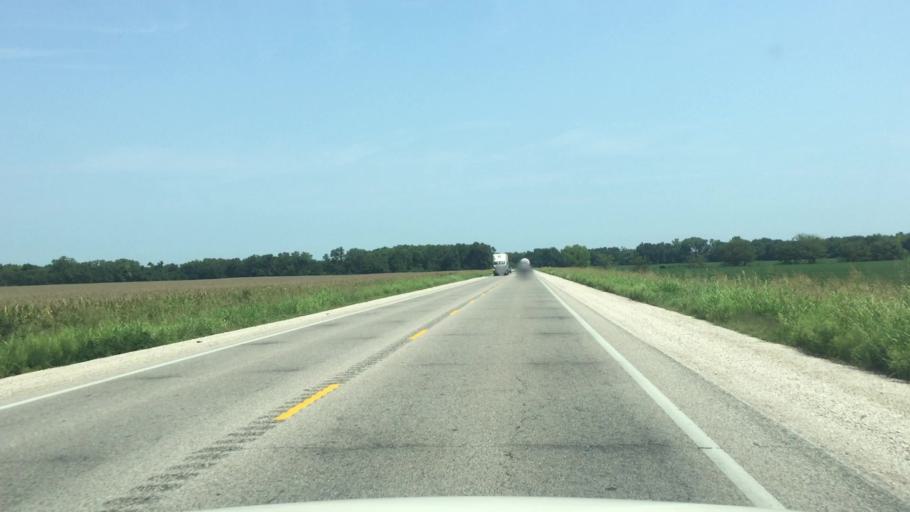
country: US
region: Kansas
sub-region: Montgomery County
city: Cherryvale
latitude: 37.1699
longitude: -95.5765
